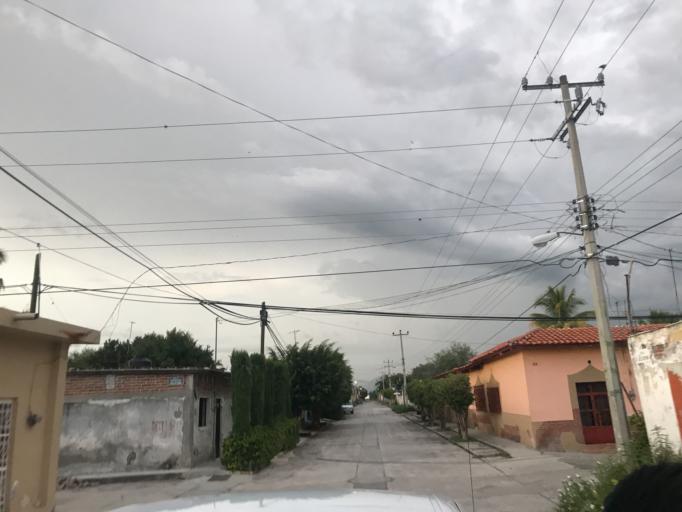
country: MX
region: Morelos
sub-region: Axochiapan
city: Quebrantadero
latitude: 18.5241
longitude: -98.7924
